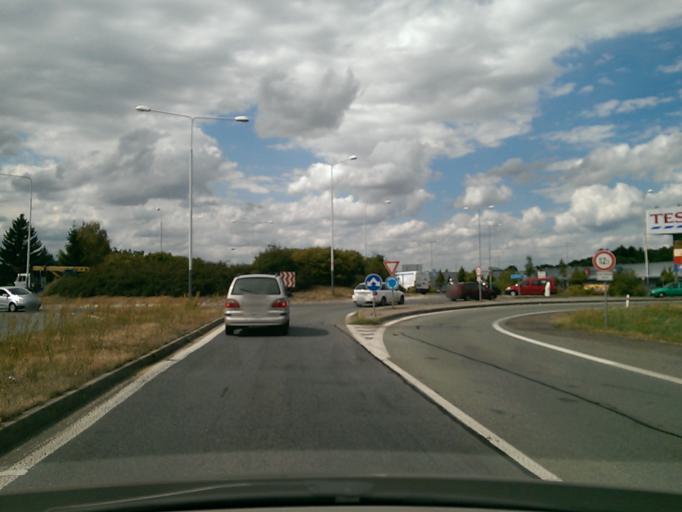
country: CZ
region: Central Bohemia
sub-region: Okres Nymburk
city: Podebrady
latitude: 50.1327
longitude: 15.0987
